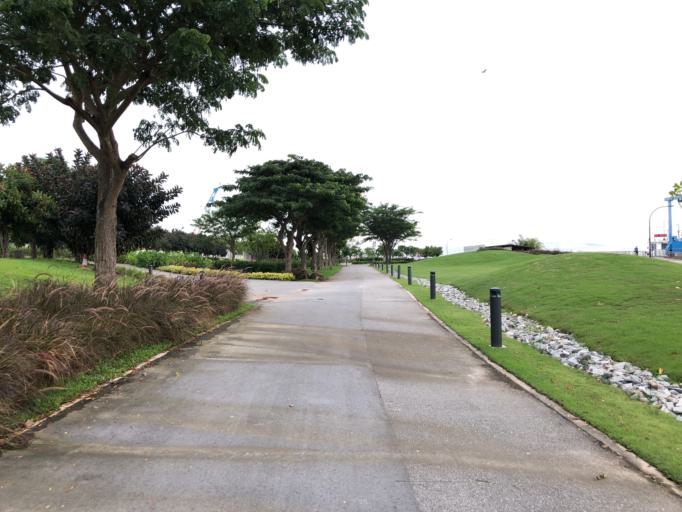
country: SG
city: Singapore
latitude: 1.2831
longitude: 103.8734
